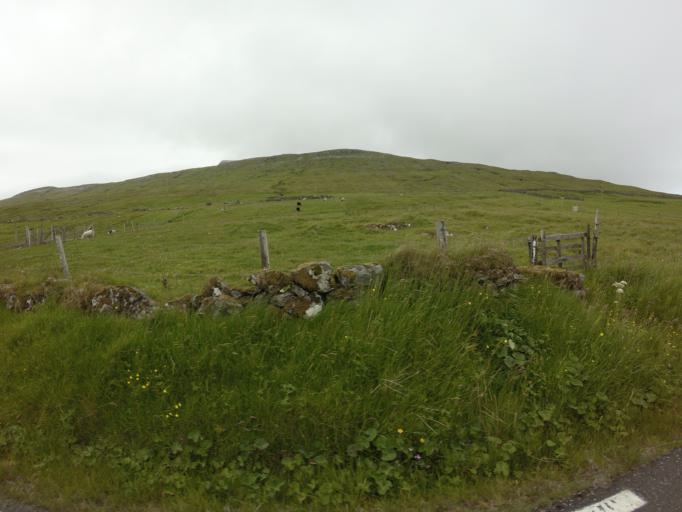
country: FO
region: Sandoy
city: Sandur
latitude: 61.8157
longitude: -6.7054
